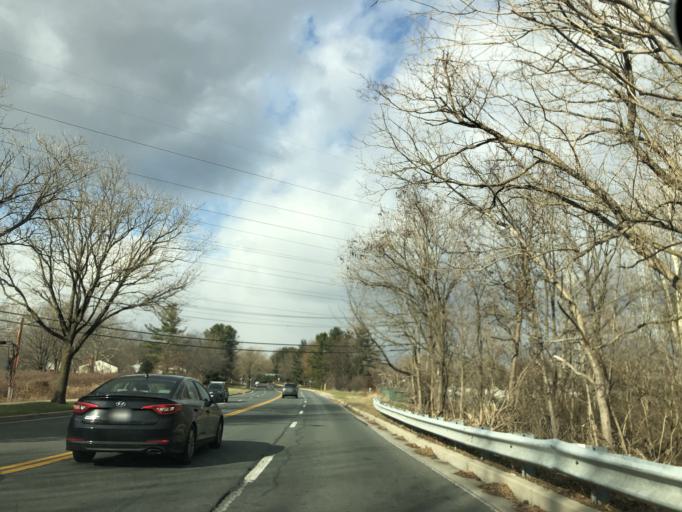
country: US
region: Maryland
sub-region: Howard County
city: Savage
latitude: 39.1883
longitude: -76.8298
